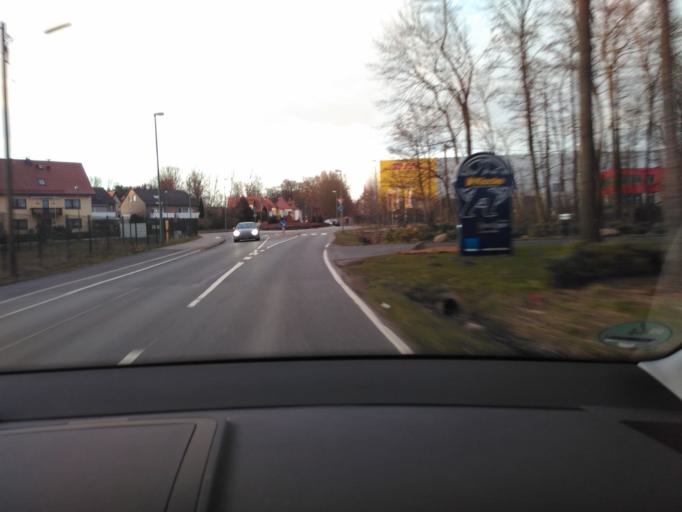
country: DE
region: North Rhine-Westphalia
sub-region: Regierungsbezirk Detmold
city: Bielefeld
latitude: 51.9698
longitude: 8.5061
